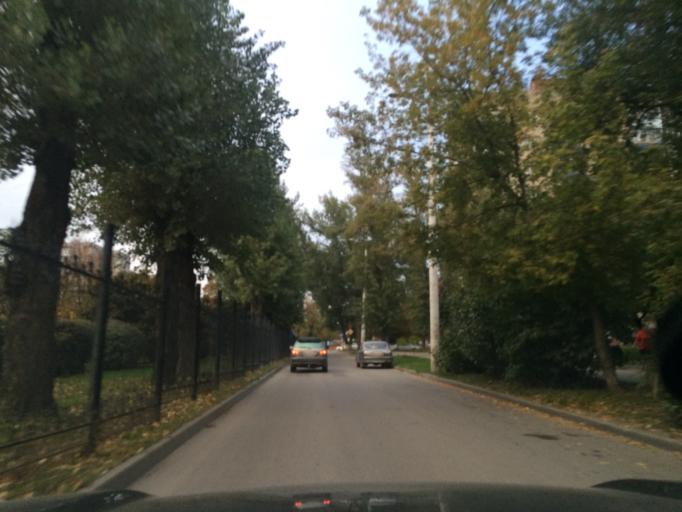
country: RU
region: Rostov
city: Rostov-na-Donu
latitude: 47.2068
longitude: 39.6338
